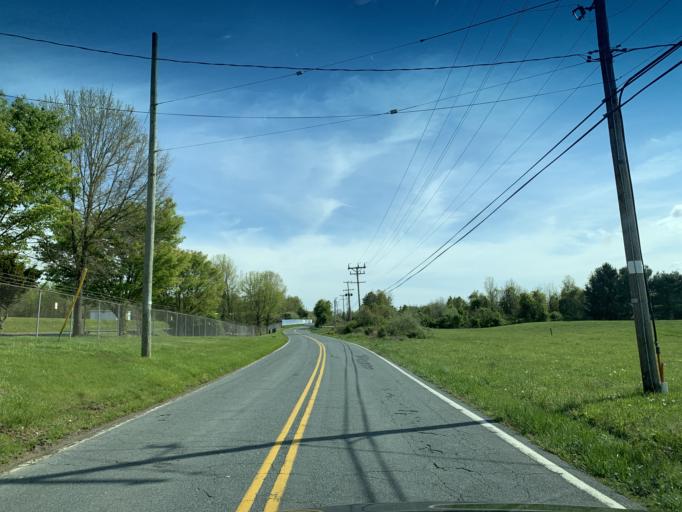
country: US
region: Maryland
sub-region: Harford County
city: Perryman
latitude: 39.4405
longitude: -76.2158
